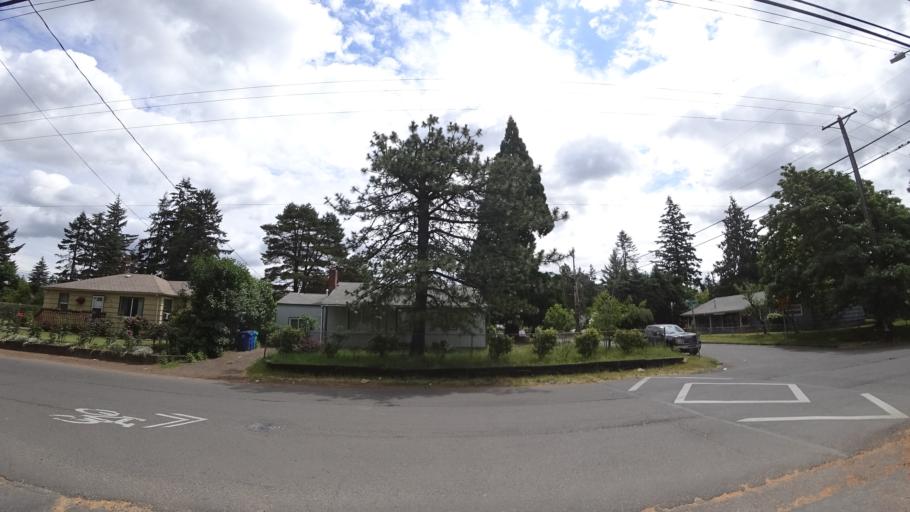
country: US
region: Oregon
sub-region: Multnomah County
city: Lents
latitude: 45.4933
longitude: -122.5301
